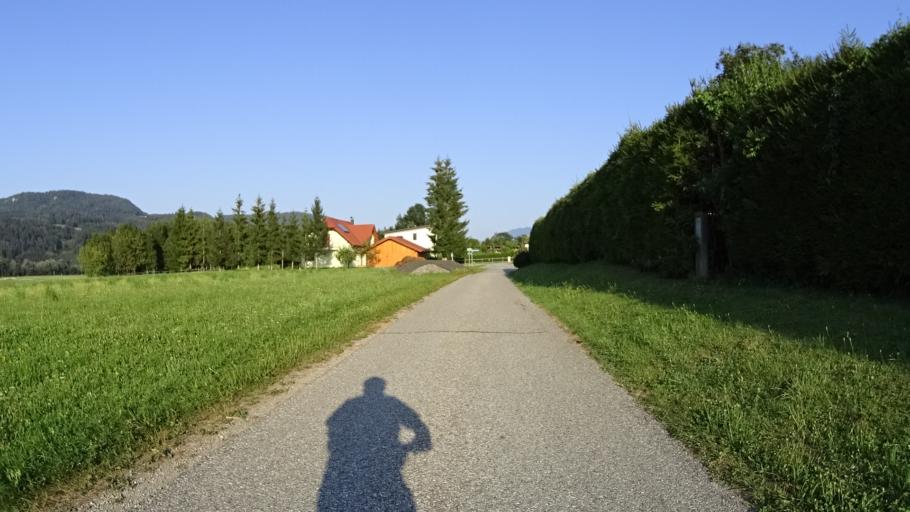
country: AT
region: Carinthia
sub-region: Politischer Bezirk Villach Land
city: Sankt Jakob
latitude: 46.5535
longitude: 14.0624
